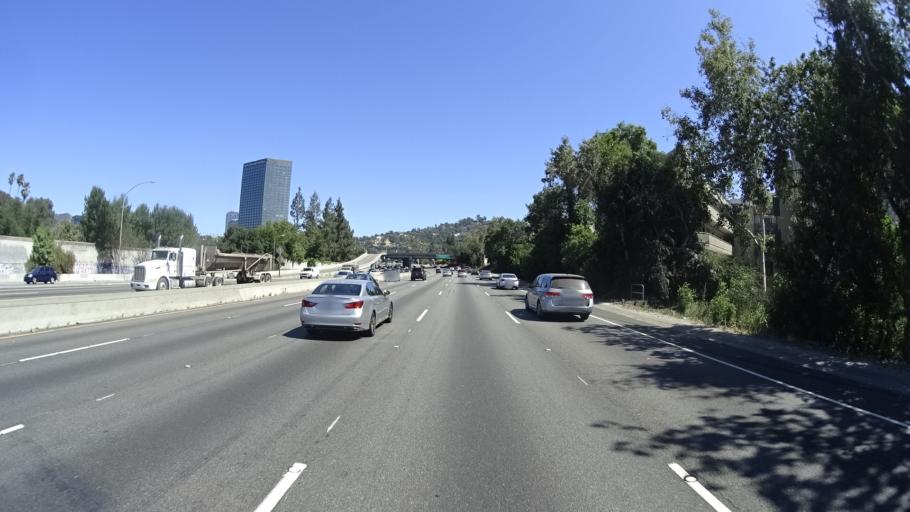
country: US
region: California
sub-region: Los Angeles County
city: Universal City
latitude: 34.1423
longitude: -118.3672
